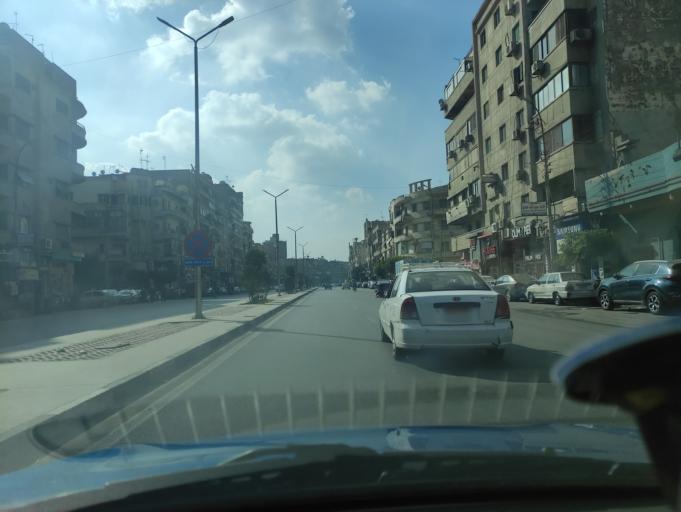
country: EG
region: Muhafazat al Qahirah
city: Cairo
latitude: 30.0993
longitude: 31.3411
